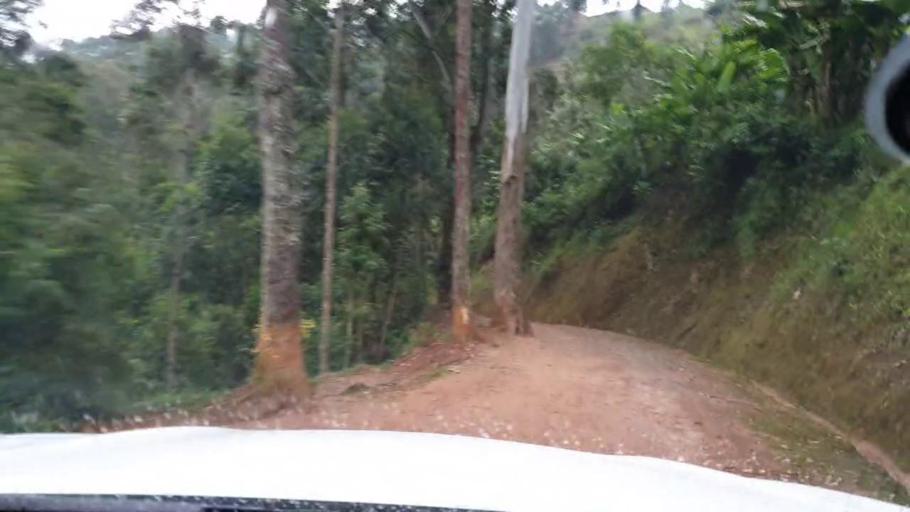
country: RW
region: Western Province
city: Cyangugu
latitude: -2.4094
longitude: 29.2016
